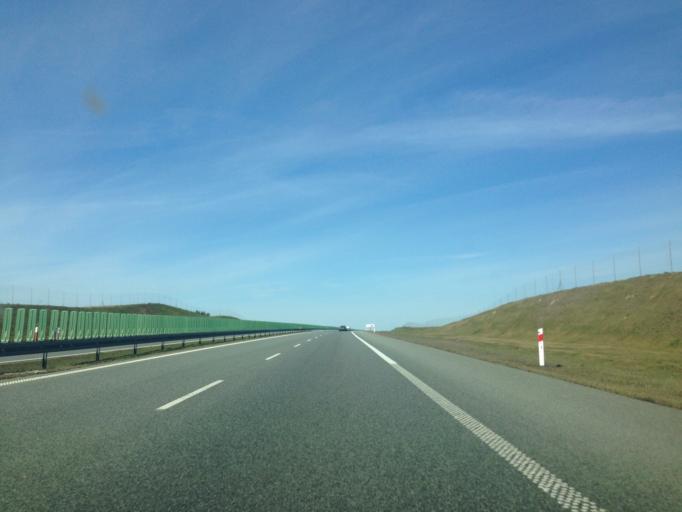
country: PL
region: Pomeranian Voivodeship
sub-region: Powiat starogardzki
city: Bobowo
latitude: 53.8430
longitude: 18.6269
